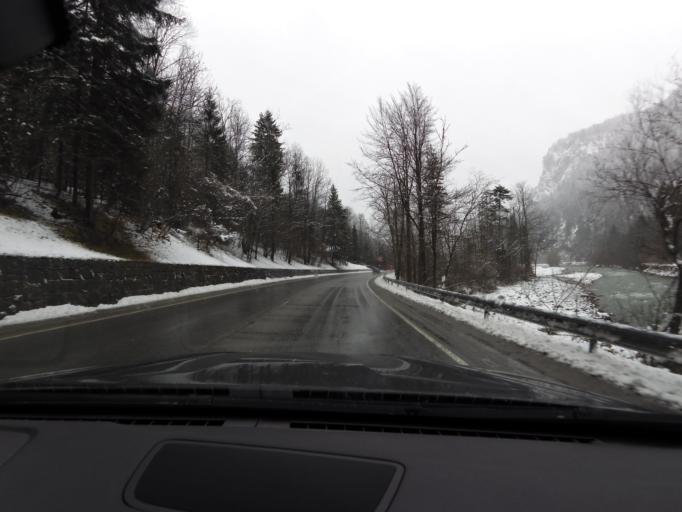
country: DE
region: Bavaria
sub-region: Upper Bavaria
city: Marktschellenberg
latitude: 47.6631
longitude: 13.0363
